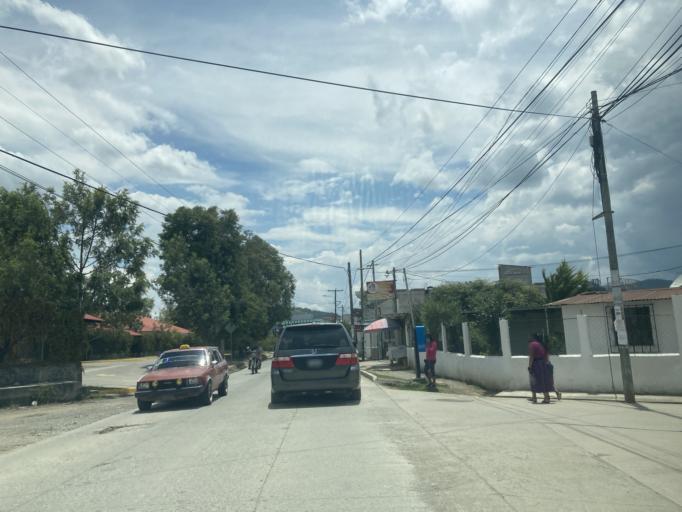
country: GT
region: Huehuetenango
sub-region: Municipio de Huehuetenango
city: Huehuetenango
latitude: 15.3226
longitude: -91.4954
